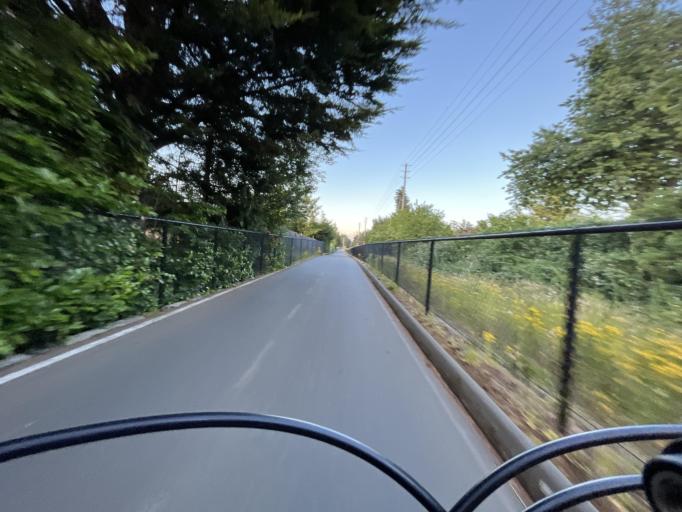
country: CA
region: British Columbia
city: Victoria
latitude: 48.4376
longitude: -123.4126
